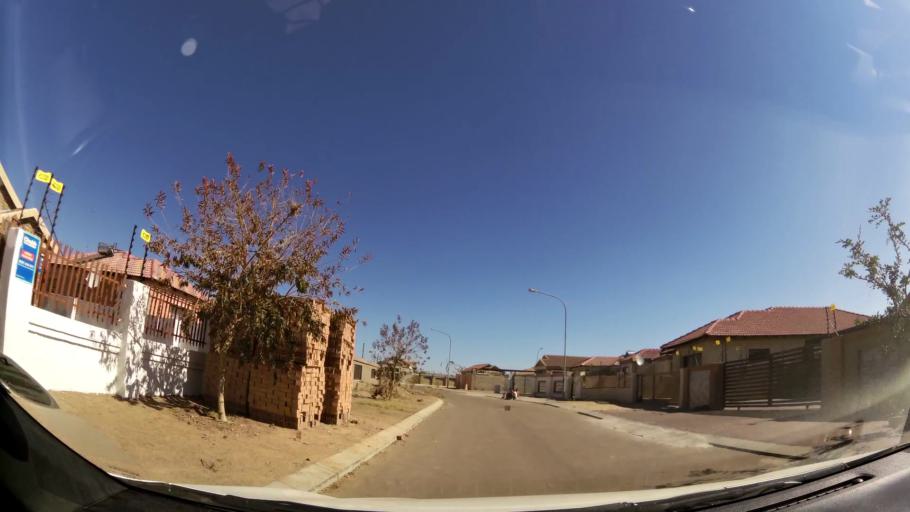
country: ZA
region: Limpopo
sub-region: Capricorn District Municipality
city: Polokwane
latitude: -23.8583
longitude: 29.4237
